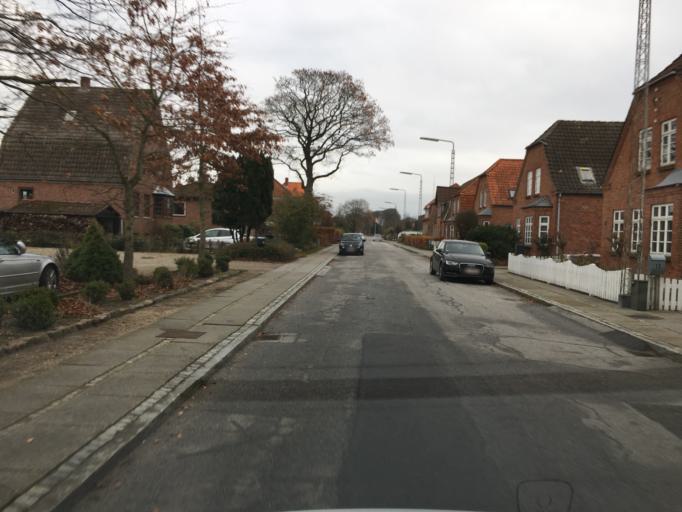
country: DK
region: South Denmark
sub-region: Tonder Kommune
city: Tonder
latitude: 54.9440
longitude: 8.8667
